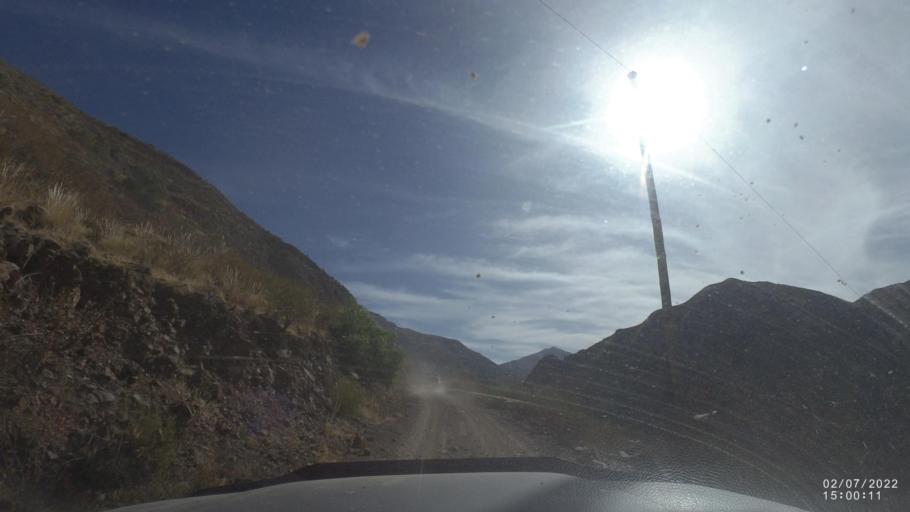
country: BO
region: Cochabamba
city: Irpa Irpa
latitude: -17.8519
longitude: -66.4423
